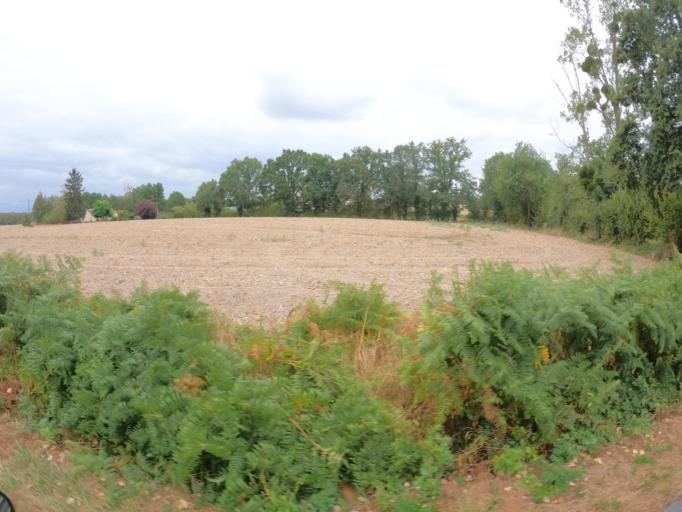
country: FR
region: Pays de la Loire
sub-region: Departement de la Vendee
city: Les Landes-Genusson
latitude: 46.9734
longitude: -1.1127
